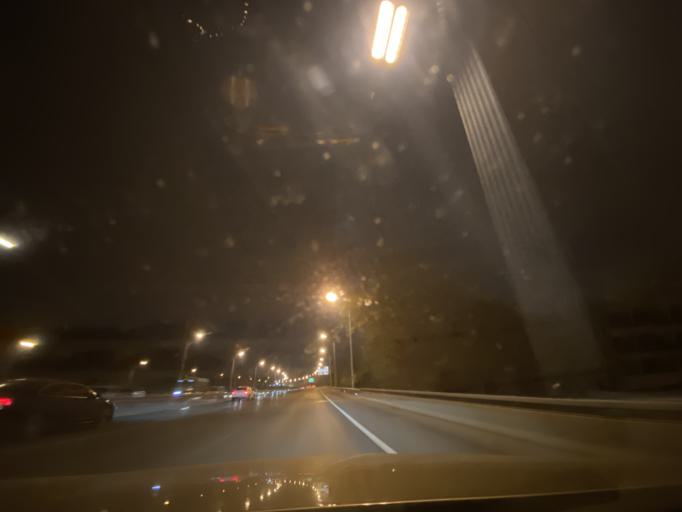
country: CN
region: Beijing
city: Xiangshan
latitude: 39.9447
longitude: 116.2073
